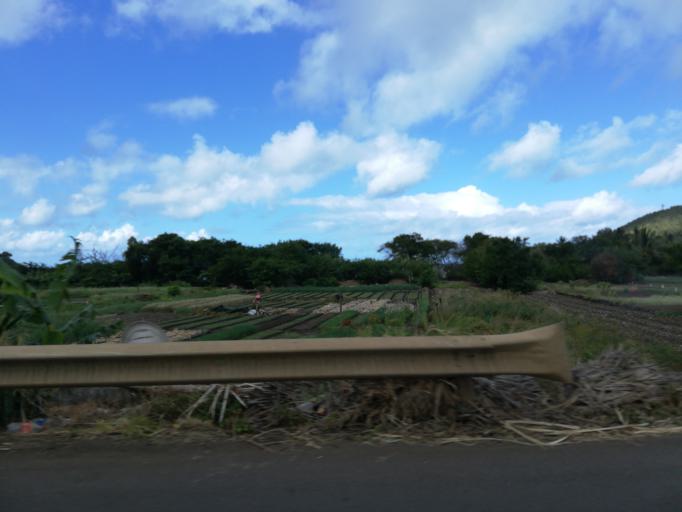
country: MU
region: Grand Port
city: Bambous Virieux
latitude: -20.3321
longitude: 57.7673
